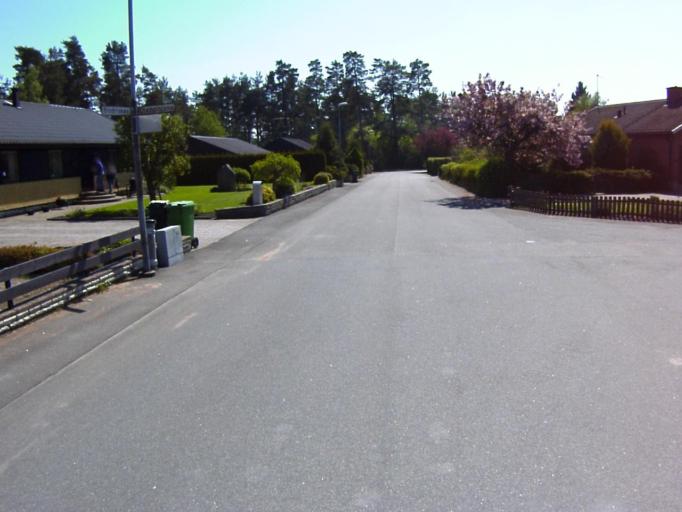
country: SE
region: Skane
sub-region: Kristianstads Kommun
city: Degeberga
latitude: 55.9018
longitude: 14.1009
